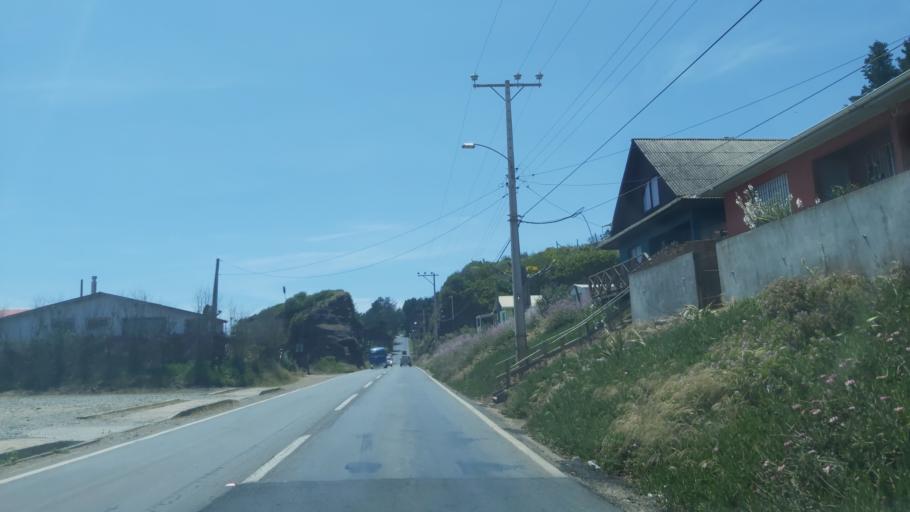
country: CL
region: Maule
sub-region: Provincia de Cauquenes
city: Cauquenes
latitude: -35.8369
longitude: -72.6247
